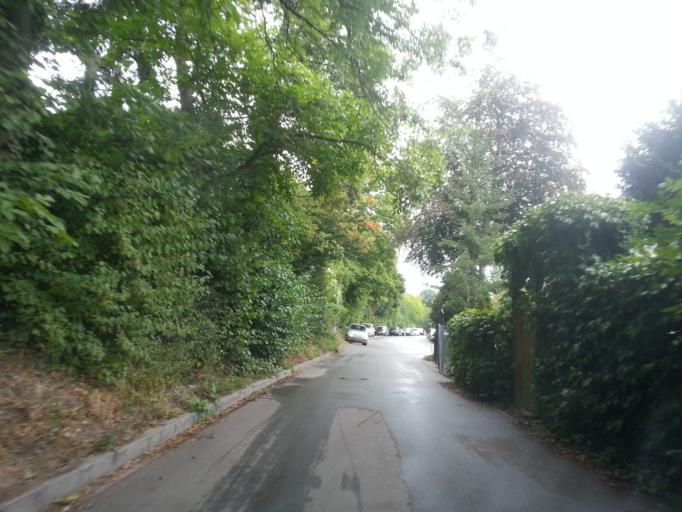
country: DE
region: Rheinland-Pfalz
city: Landau in der Pfalz
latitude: 49.1989
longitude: 8.1013
